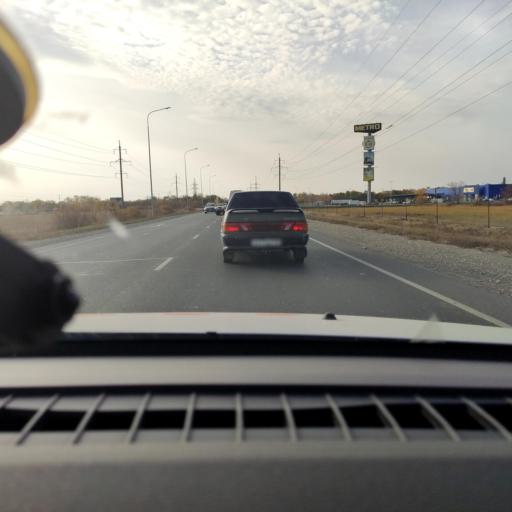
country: RU
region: Samara
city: Samara
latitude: 53.1313
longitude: 50.1431
